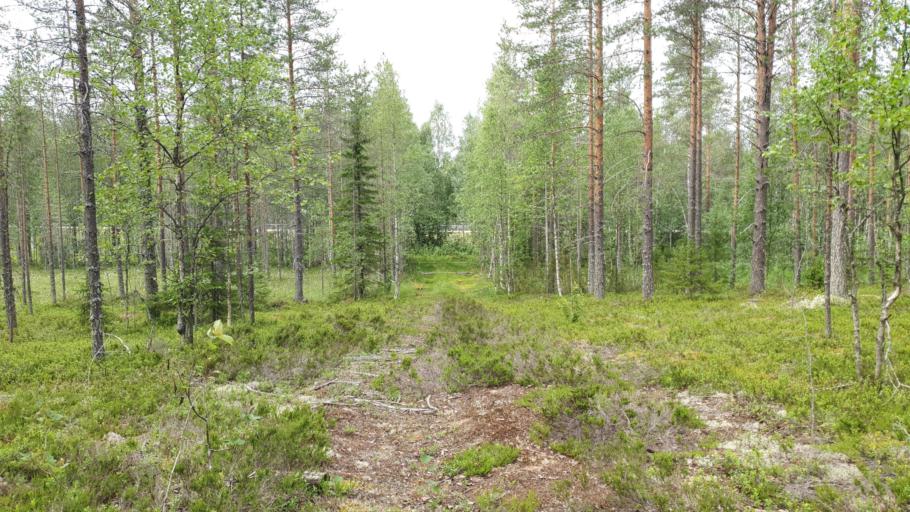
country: FI
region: Kainuu
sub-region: Kehys-Kainuu
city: Kuhmo
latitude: 63.9386
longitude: 29.5988
